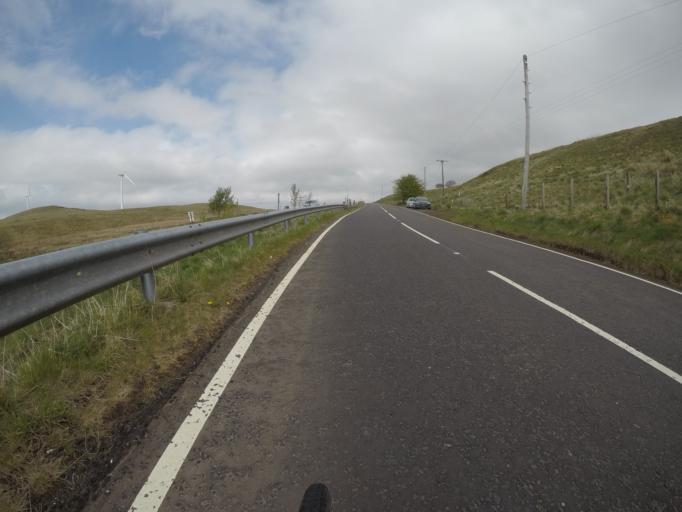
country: GB
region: Scotland
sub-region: East Renfrewshire
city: Neilston
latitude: 55.7411
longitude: -4.4055
